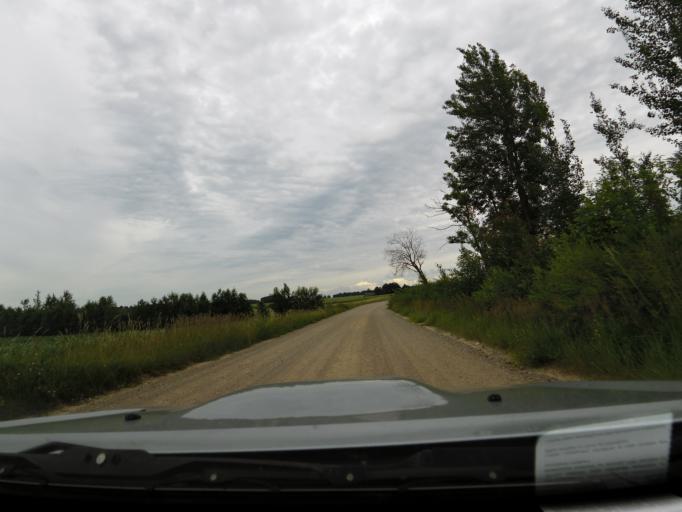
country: LV
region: Rundales
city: Pilsrundale
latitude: 56.4905
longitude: 24.0888
